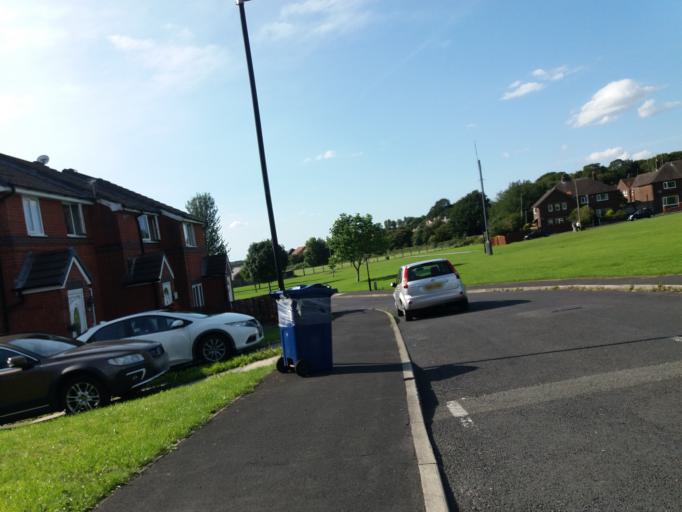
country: GB
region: England
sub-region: Lancashire
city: Coppull
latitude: 53.6425
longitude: -2.6445
